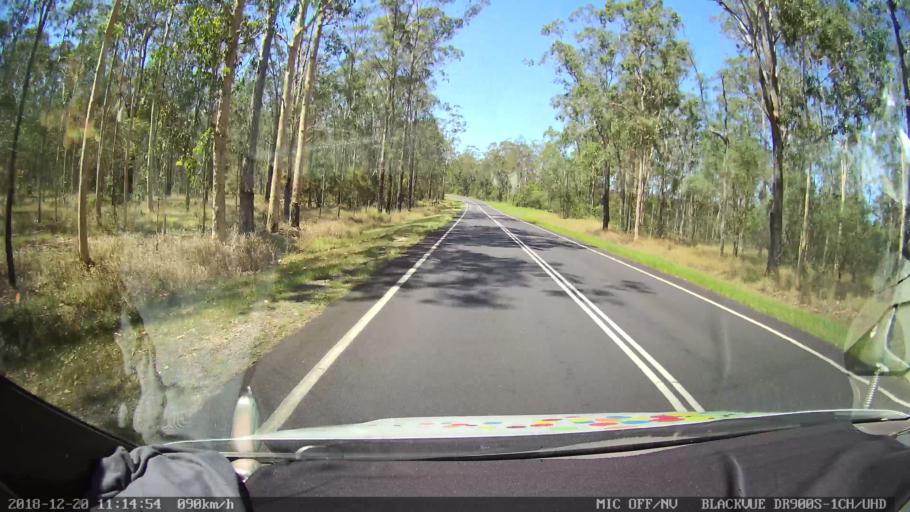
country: AU
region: New South Wales
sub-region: Richmond Valley
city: Casino
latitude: -29.0063
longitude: 153.0070
